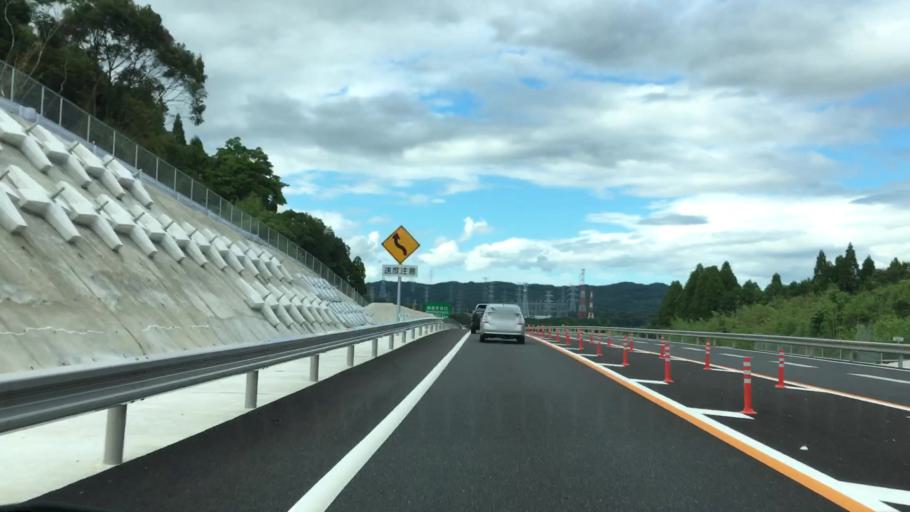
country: JP
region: Saga Prefecture
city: Imaricho-ko
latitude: 33.3322
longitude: 129.9279
